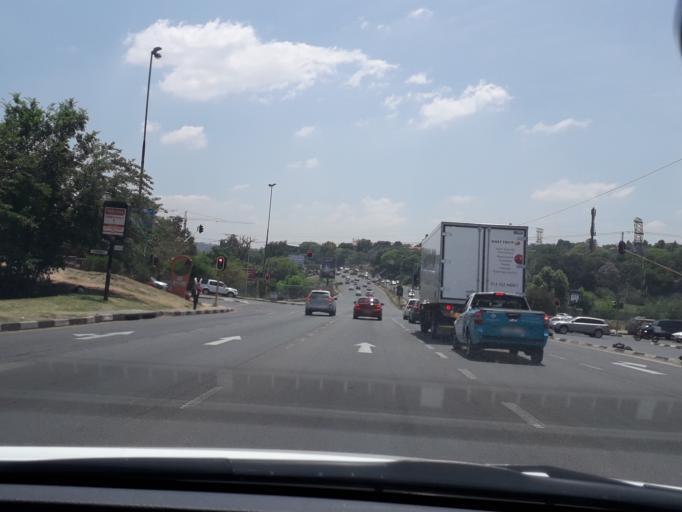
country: ZA
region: Gauteng
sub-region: City of Johannesburg Metropolitan Municipality
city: Johannesburg
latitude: -26.1009
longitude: 28.0324
